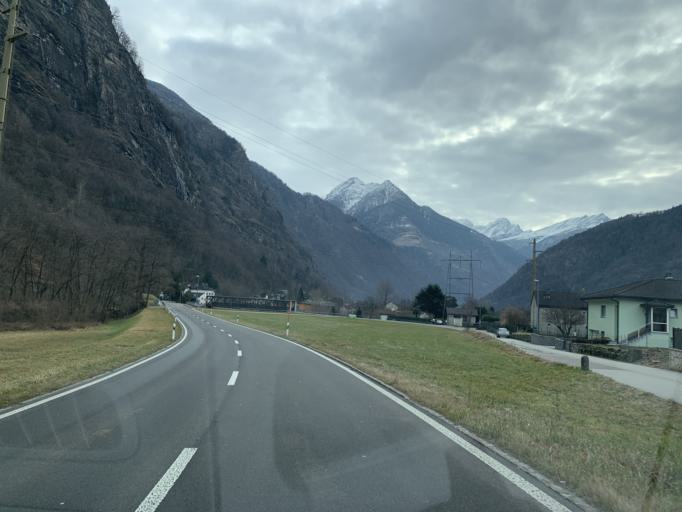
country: CH
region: Ticino
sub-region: Blenio District
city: Acquarossa
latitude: 46.4432
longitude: 8.9465
